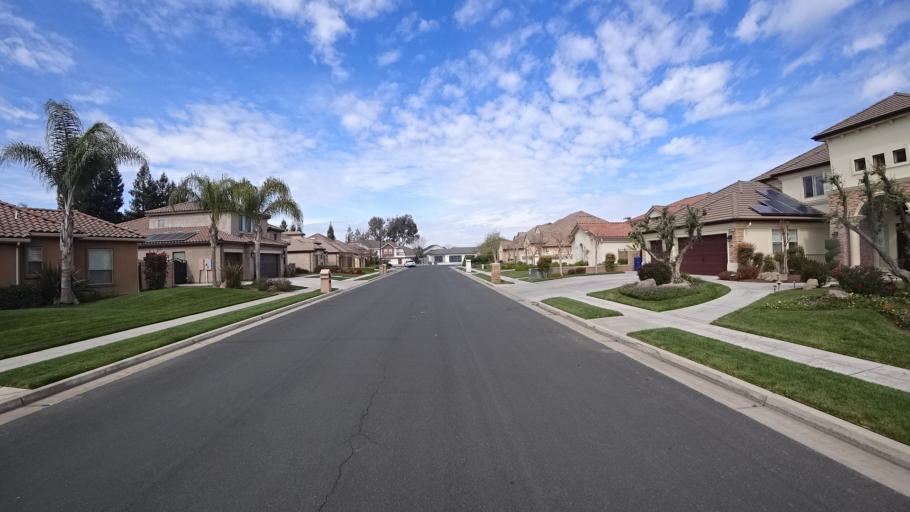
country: US
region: California
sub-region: Madera County
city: Bonadelle Ranchos-Madera Ranchos
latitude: 36.8489
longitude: -119.8830
